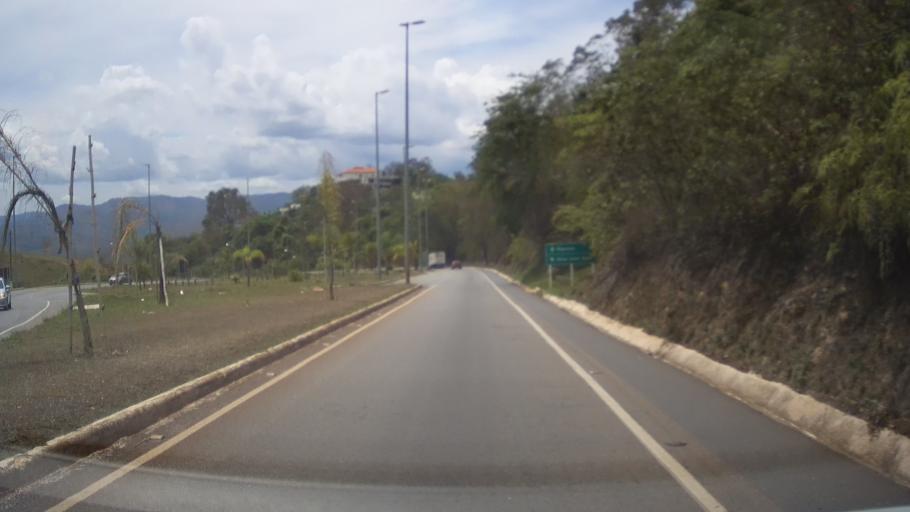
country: BR
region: Minas Gerais
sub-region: Nova Lima
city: Nova Lima
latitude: -19.9891
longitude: -43.8643
